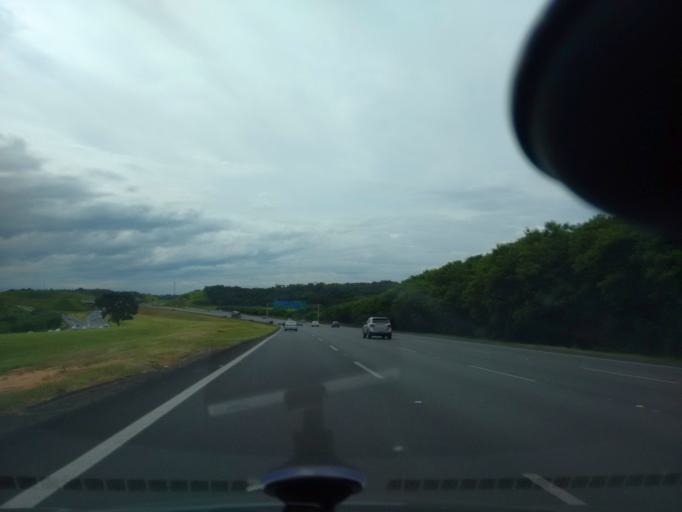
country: BR
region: Sao Paulo
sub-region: Campinas
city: Campinas
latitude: -22.9270
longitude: -47.1294
